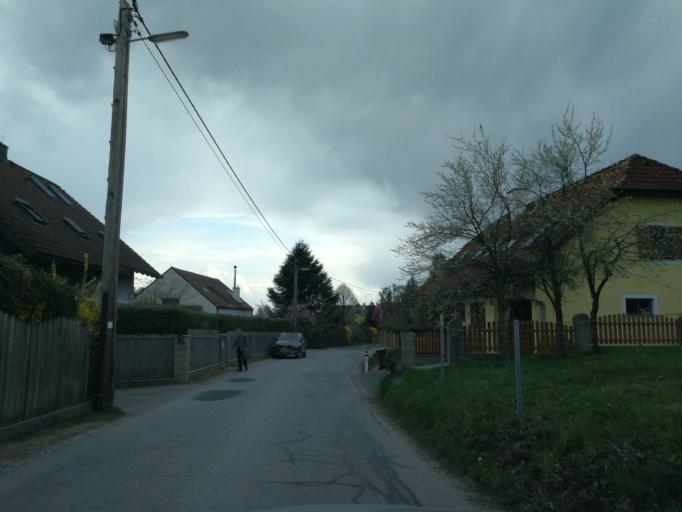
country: AT
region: Styria
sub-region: Politischer Bezirk Graz-Umgebung
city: Hart bei Graz
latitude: 47.0648
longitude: 15.5051
